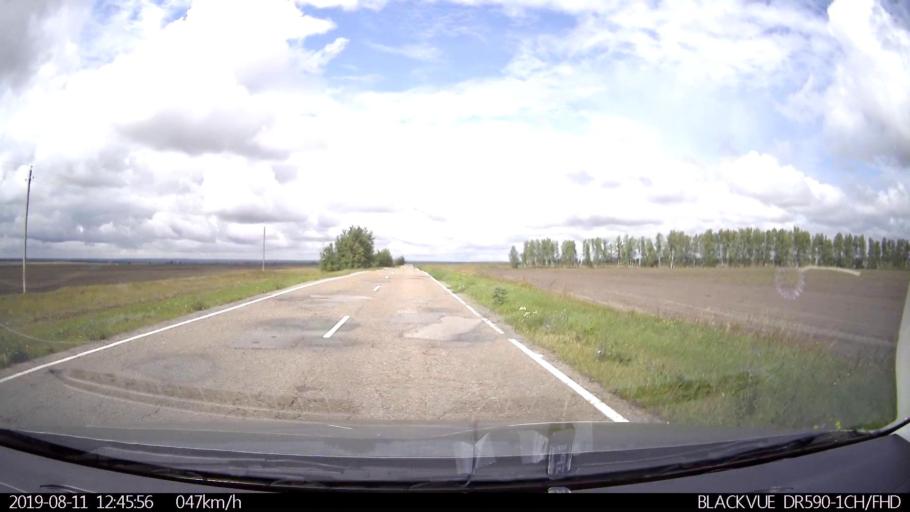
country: RU
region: Ulyanovsk
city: Ignatovka
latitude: 53.8618
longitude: 47.7235
